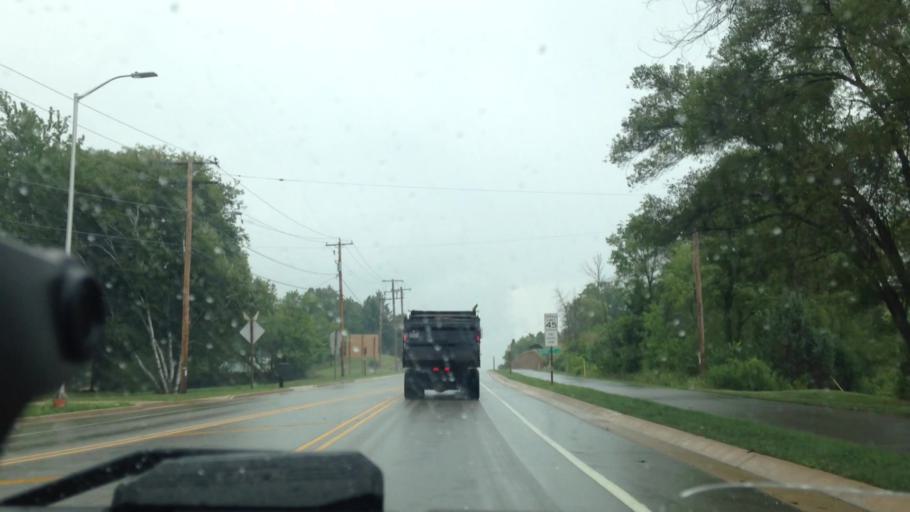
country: US
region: Wisconsin
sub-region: Washington County
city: Richfield
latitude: 43.2500
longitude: -88.1910
